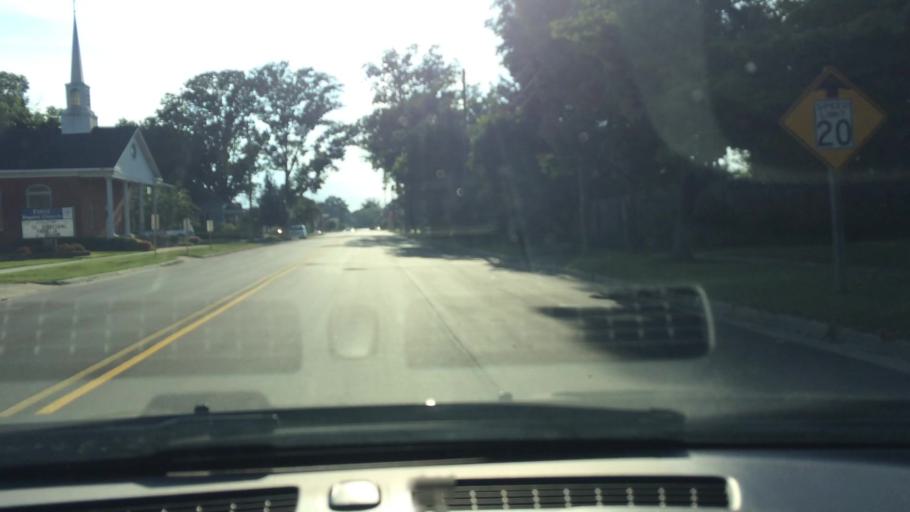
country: US
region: North Carolina
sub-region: Pitt County
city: Ayden
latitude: 35.4709
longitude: -77.4138
